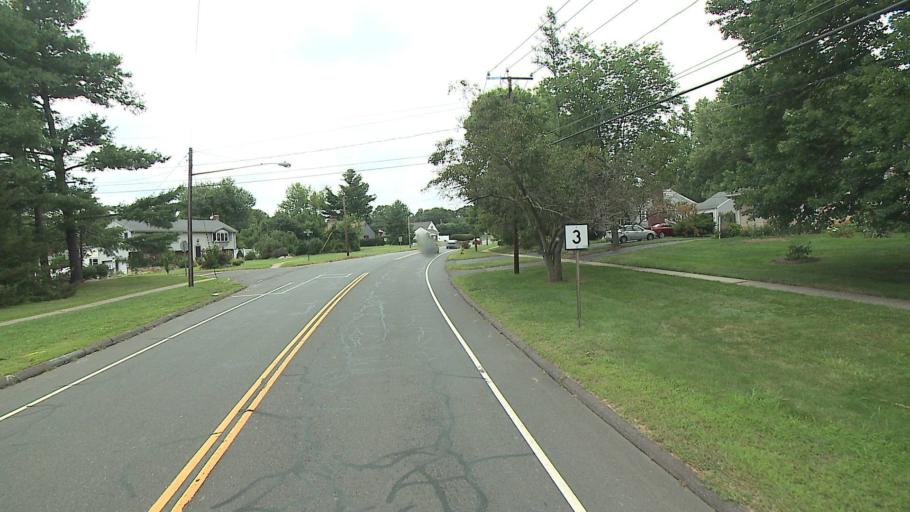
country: US
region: Connecticut
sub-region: Hartford County
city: Wethersfield
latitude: 41.6909
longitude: -72.6592
